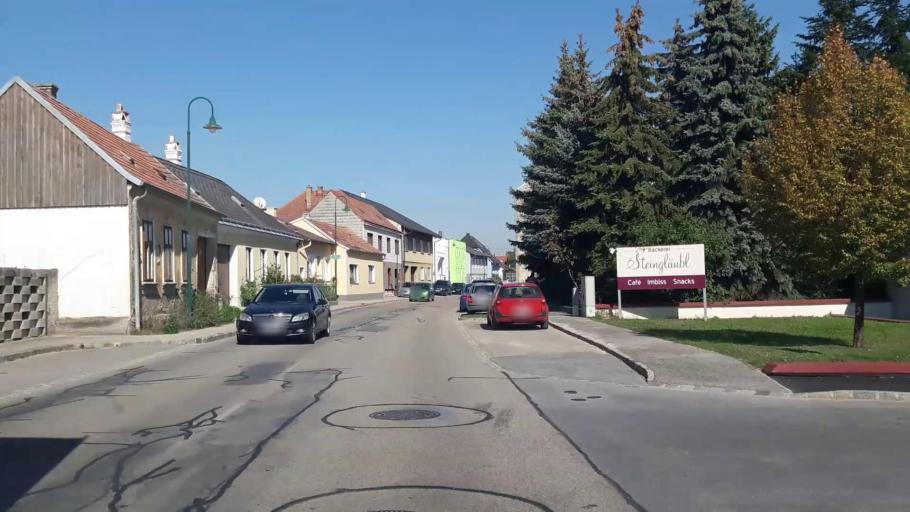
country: AT
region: Lower Austria
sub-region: Politischer Bezirk Korneuburg
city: Harmannsdorf
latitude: 48.3930
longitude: 16.3685
